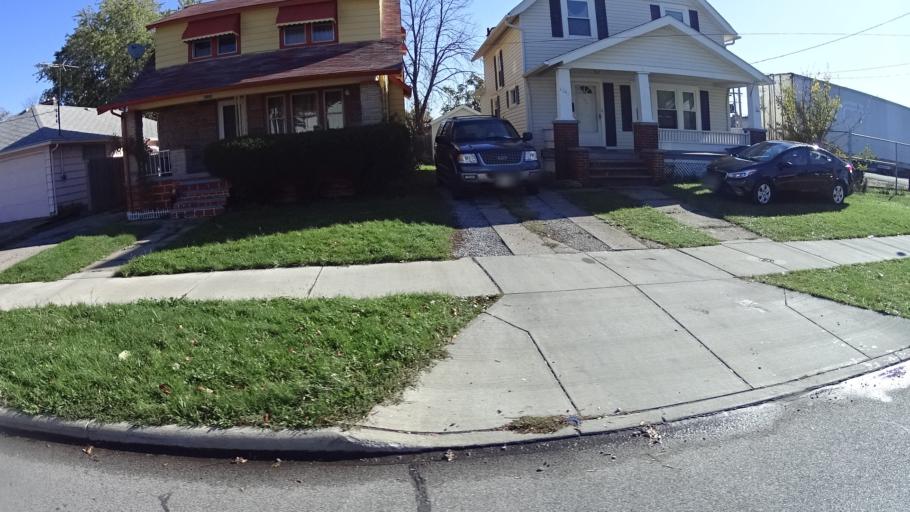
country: US
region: Ohio
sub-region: Lorain County
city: Lorain
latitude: 41.4574
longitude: -82.1850
